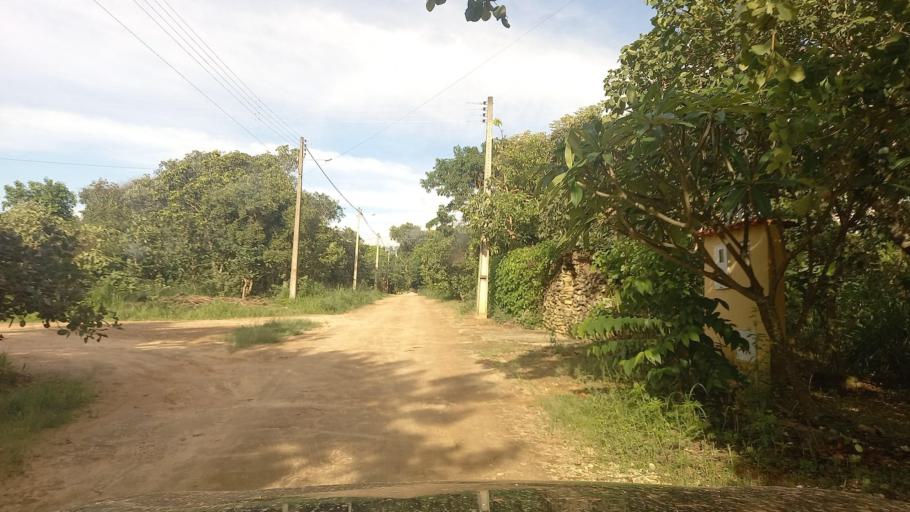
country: BR
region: Goias
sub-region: Cavalcante
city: Cavalcante
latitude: -13.7999
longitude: -47.4407
